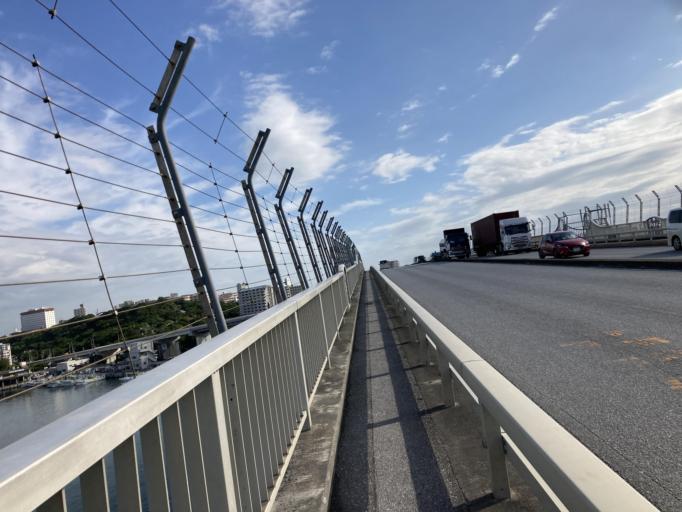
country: JP
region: Okinawa
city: Naha-shi
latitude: 26.2257
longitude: 127.6788
